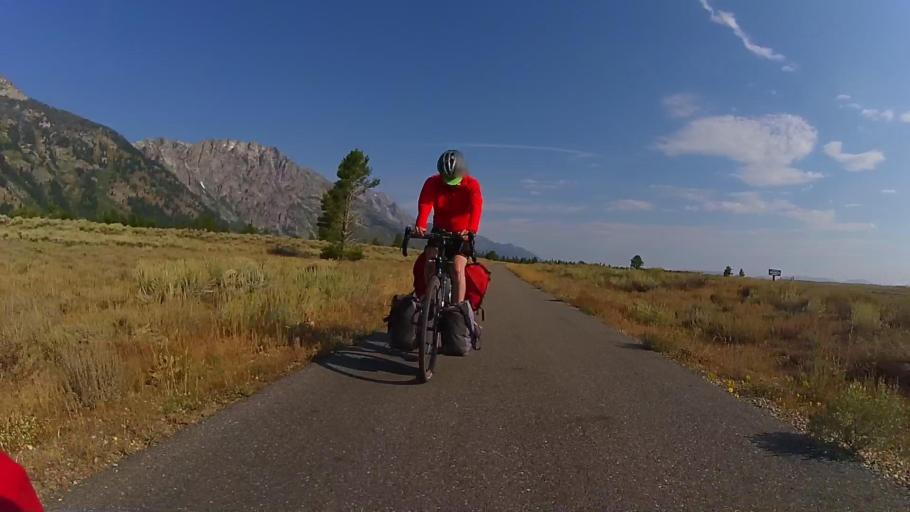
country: US
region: Wyoming
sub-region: Teton County
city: Moose Wilson Road
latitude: 43.7415
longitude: -110.7248
